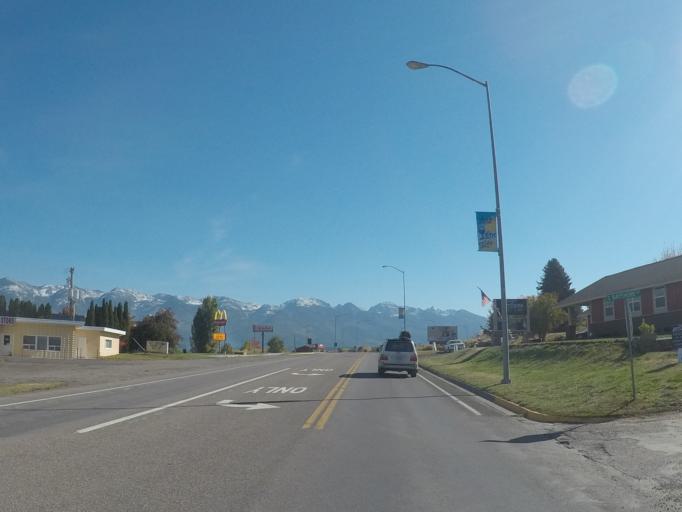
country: US
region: Montana
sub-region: Lake County
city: Polson
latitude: 47.6924
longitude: -114.1295
